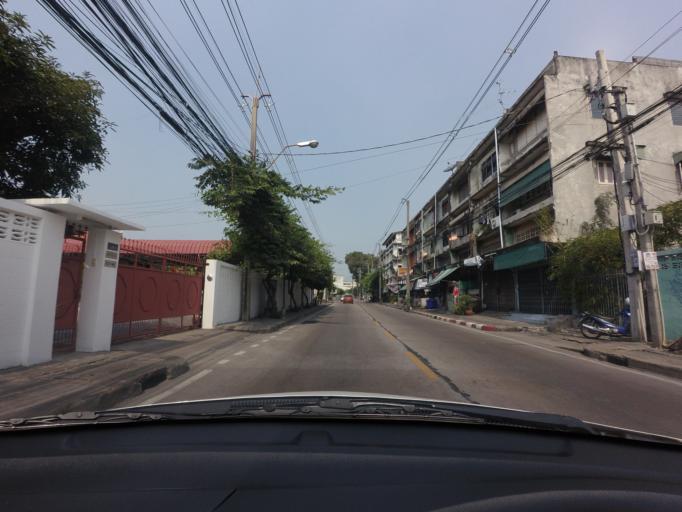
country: TH
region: Bangkok
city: Taling Chan
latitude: 13.7831
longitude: 100.4643
